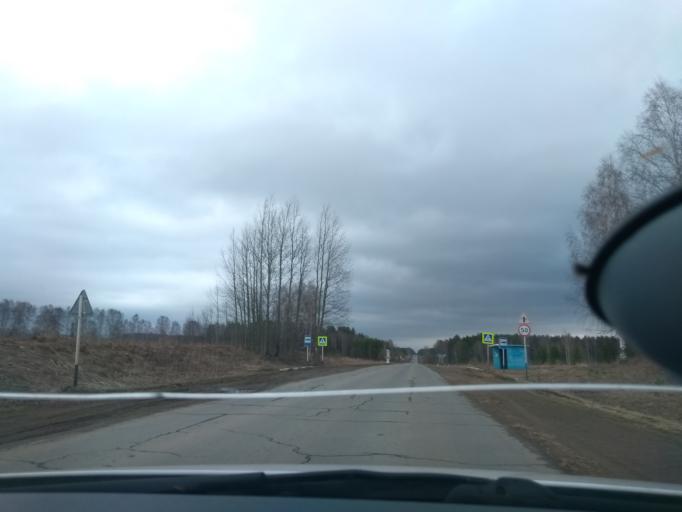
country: RU
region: Perm
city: Orda
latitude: 57.3418
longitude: 56.7842
